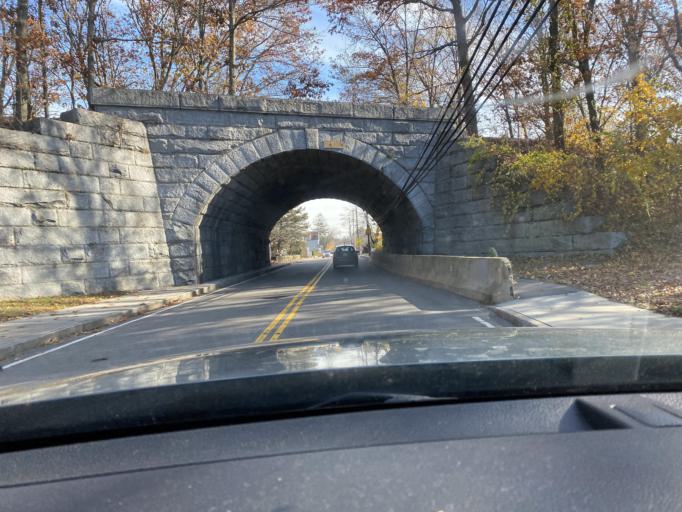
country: US
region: Massachusetts
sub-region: Norfolk County
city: Norwood
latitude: 42.1798
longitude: -71.2017
